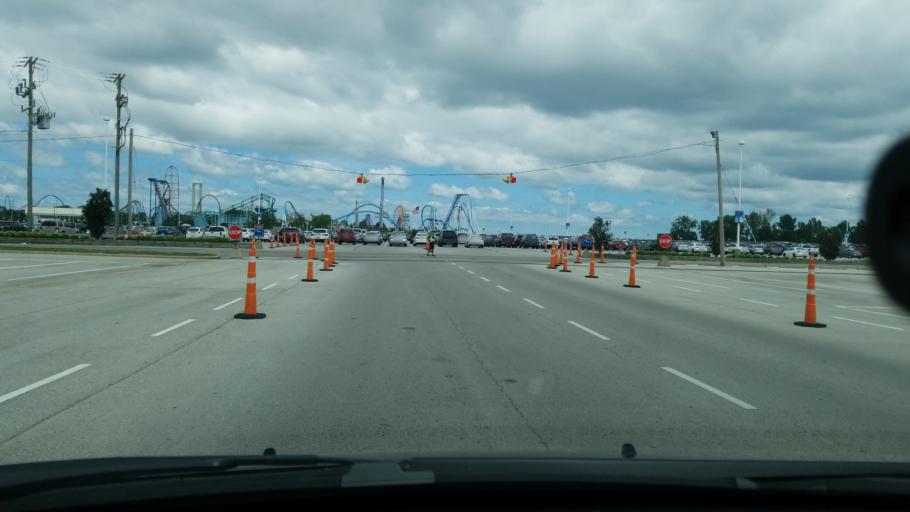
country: US
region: Ohio
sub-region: Erie County
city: Sandusky
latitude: 41.4727
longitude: -82.6768
